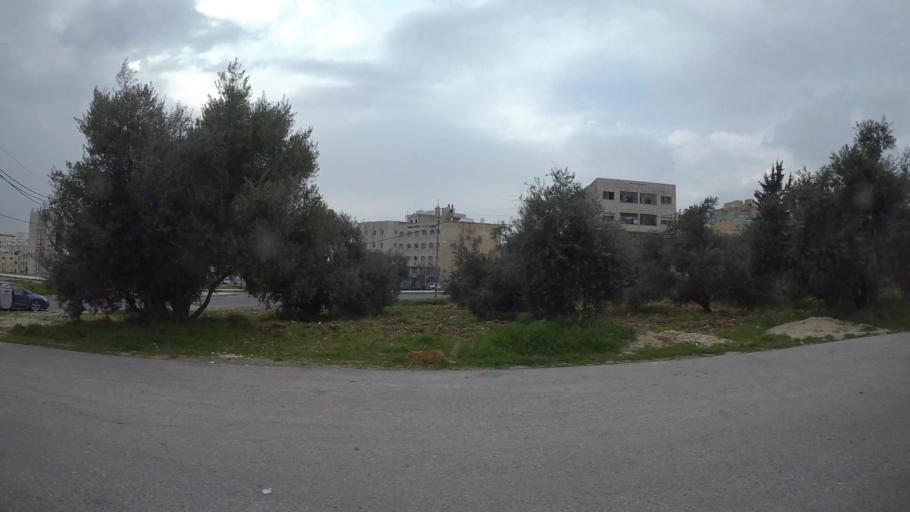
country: JO
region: Amman
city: Umm as Summaq
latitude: 31.8860
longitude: 35.8568
